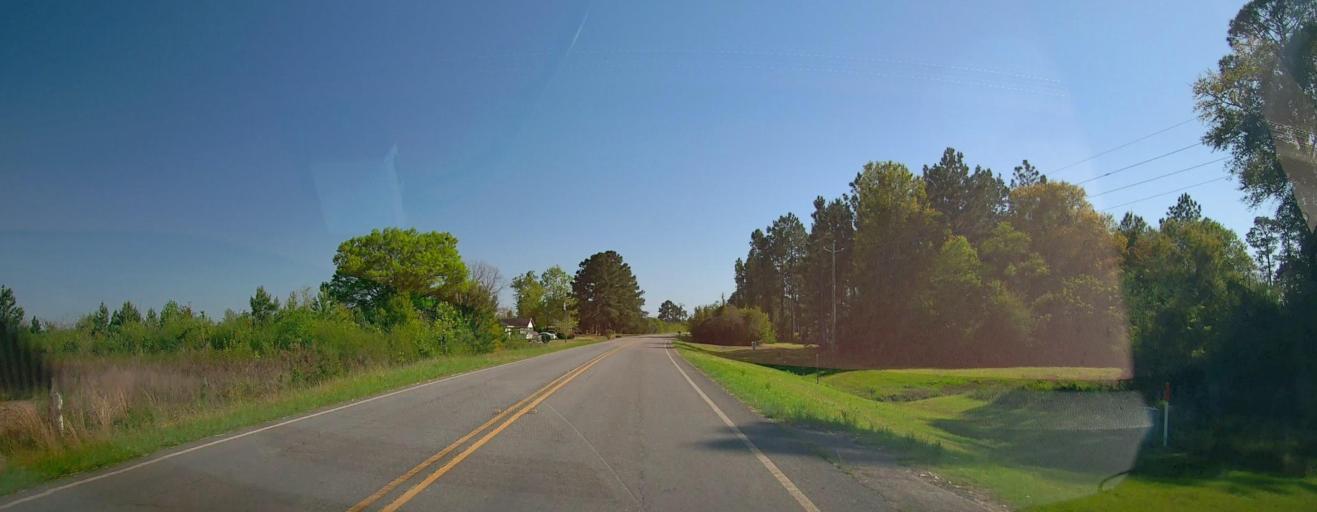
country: US
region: Georgia
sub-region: Wilcox County
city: Rochelle
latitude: 32.1060
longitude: -83.5013
